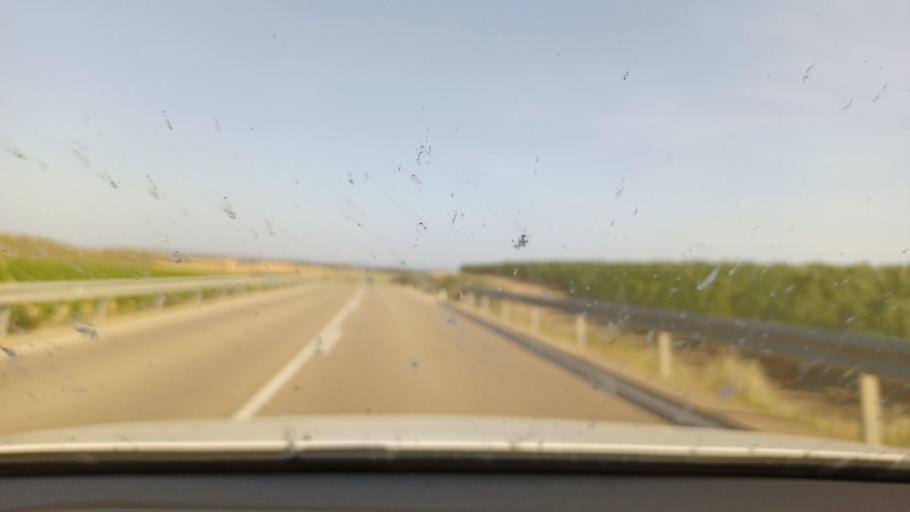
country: ES
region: Aragon
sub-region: Provincia de Zaragoza
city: Chiprana
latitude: 41.3081
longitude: -0.0737
